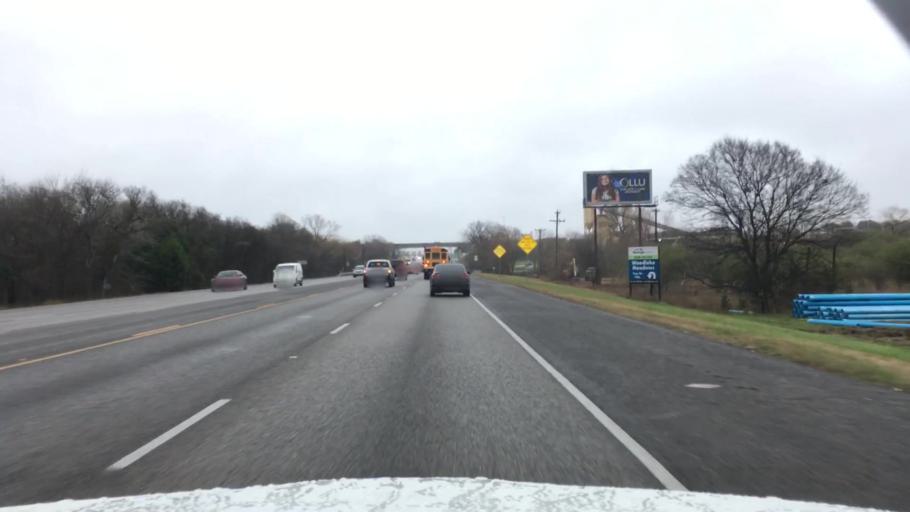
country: US
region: Texas
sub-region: Bexar County
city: Converse
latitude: 29.5298
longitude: -98.3055
